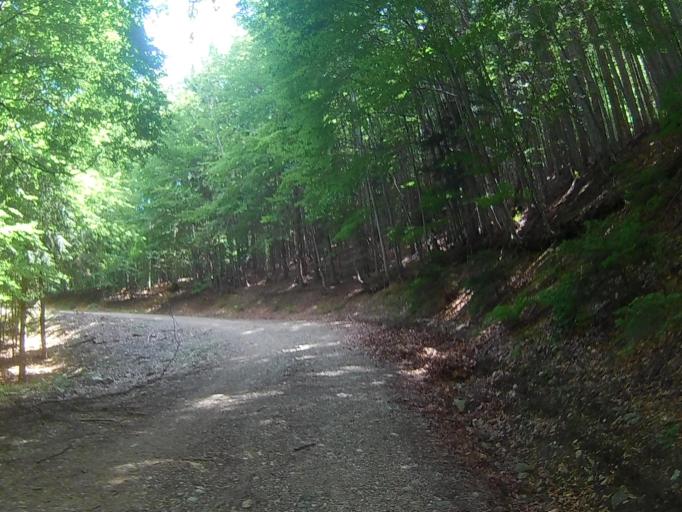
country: SI
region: Selnica ob Dravi
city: Selnica ob Dravi
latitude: 46.5101
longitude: 15.4783
